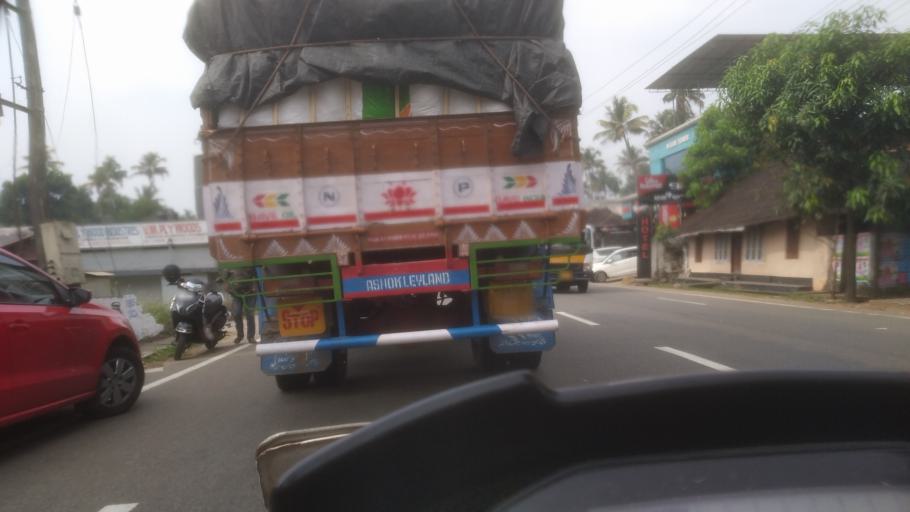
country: IN
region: Kerala
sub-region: Ernakulam
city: Perumpavur
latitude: 10.1294
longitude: 76.4709
